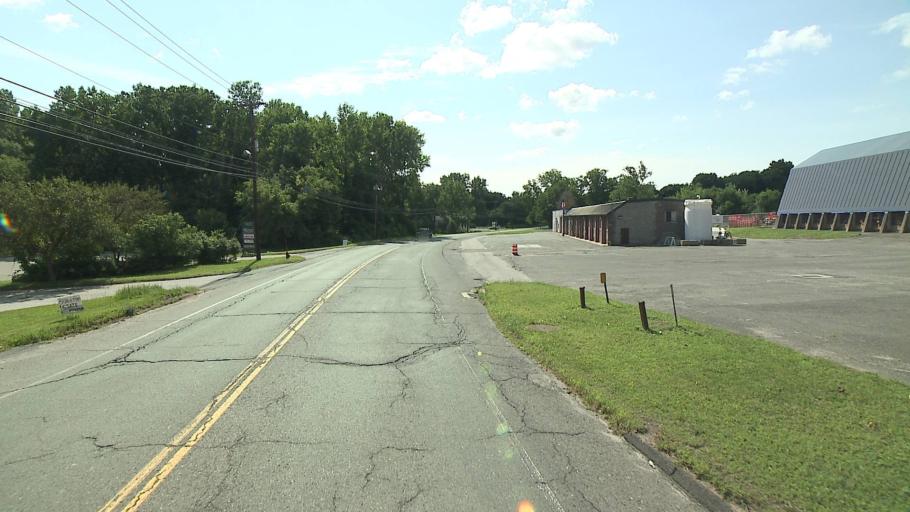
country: US
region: Connecticut
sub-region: Litchfield County
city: New Milford
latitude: 41.5790
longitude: -73.4225
